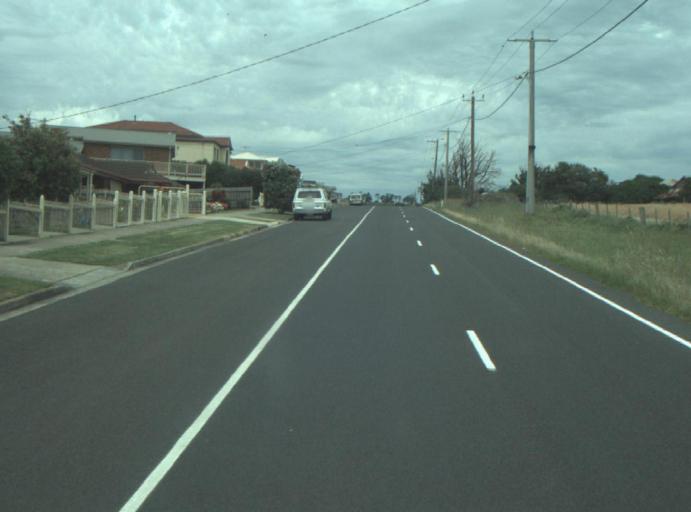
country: AU
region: Victoria
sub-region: Greater Geelong
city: Clifton Springs
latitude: -38.1222
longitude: 144.6275
